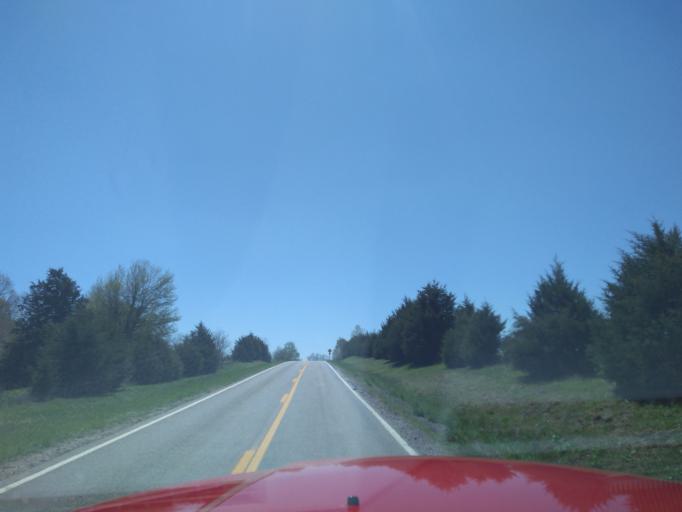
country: US
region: Arkansas
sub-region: Washington County
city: West Fork
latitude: 35.8284
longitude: -94.2662
